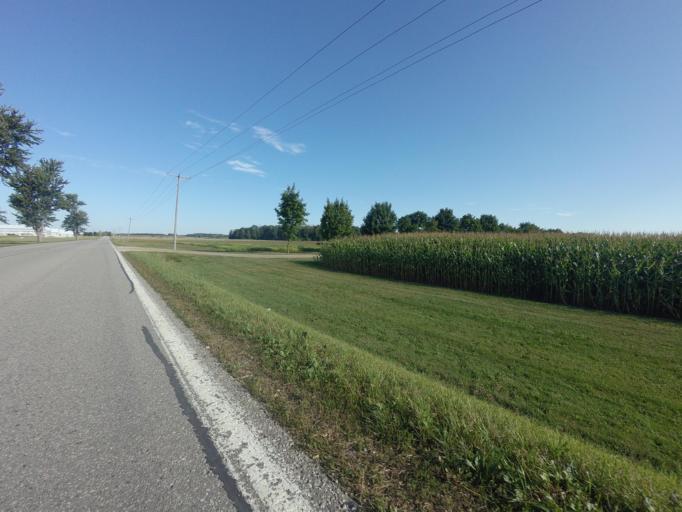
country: CA
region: Ontario
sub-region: Wellington County
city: Guelph
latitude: 43.6431
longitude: -80.4053
